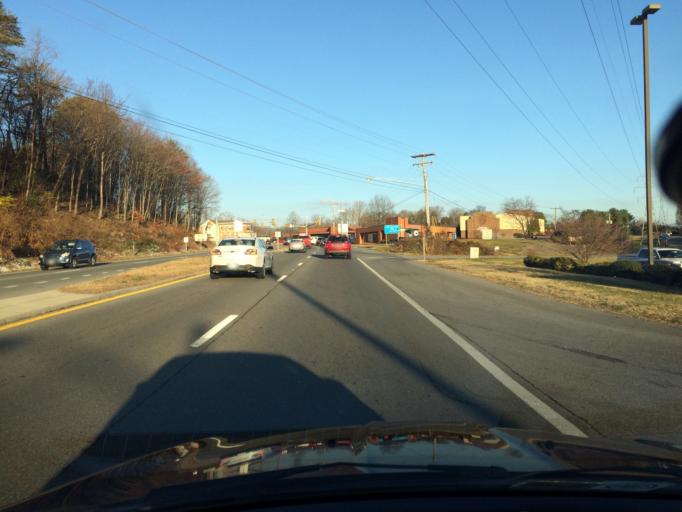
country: US
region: Virginia
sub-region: Roanoke County
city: Cave Spring
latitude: 37.2311
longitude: -80.0094
